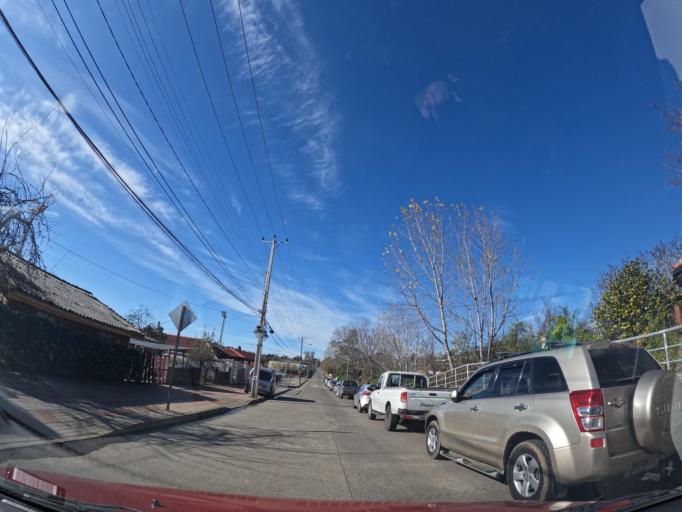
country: CL
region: Biobio
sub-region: Provincia de Biobio
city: Yumbel
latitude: -36.8249
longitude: -72.6684
